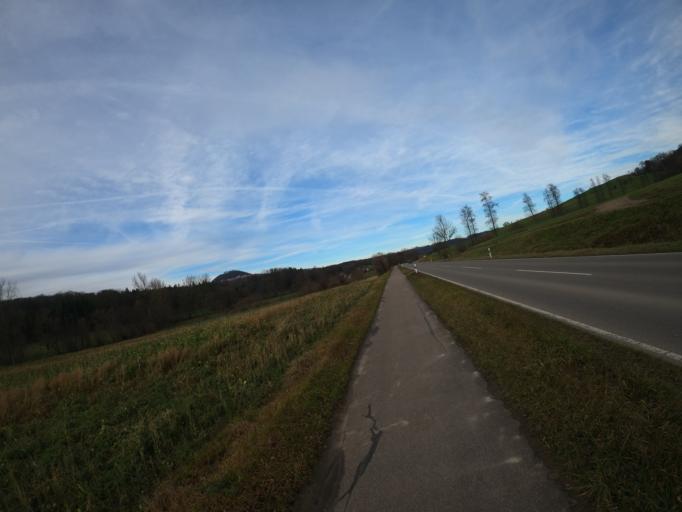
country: DE
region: Baden-Wuerttemberg
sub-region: Regierungsbezirk Stuttgart
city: Ottenbach
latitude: 48.7163
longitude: 9.7356
